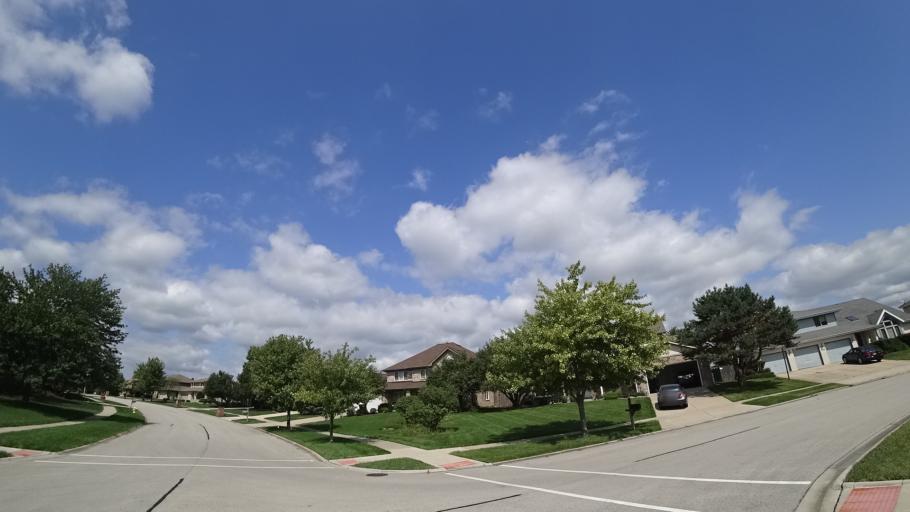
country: US
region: Illinois
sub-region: Will County
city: Mokena
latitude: 41.5636
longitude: -87.8782
